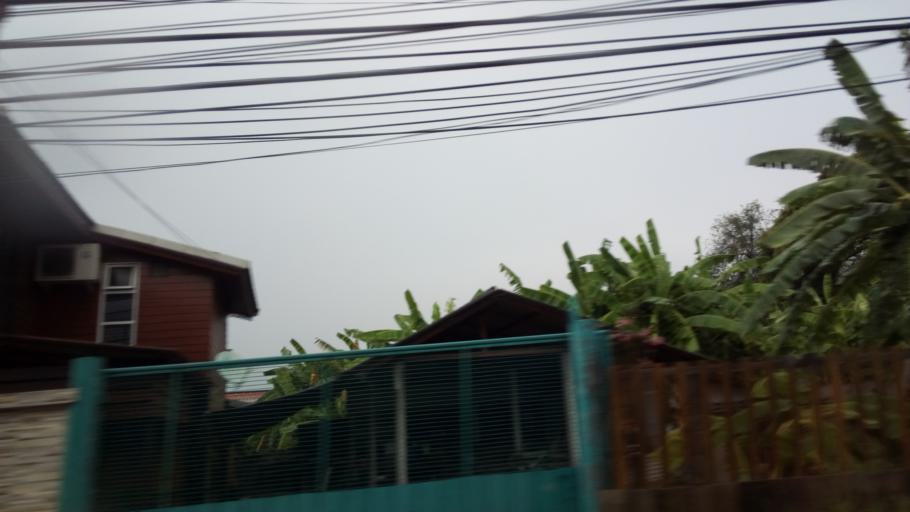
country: TH
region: Phra Nakhon Si Ayutthaya
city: Phra Nakhon Si Ayutthaya
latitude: 14.3486
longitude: 100.5423
